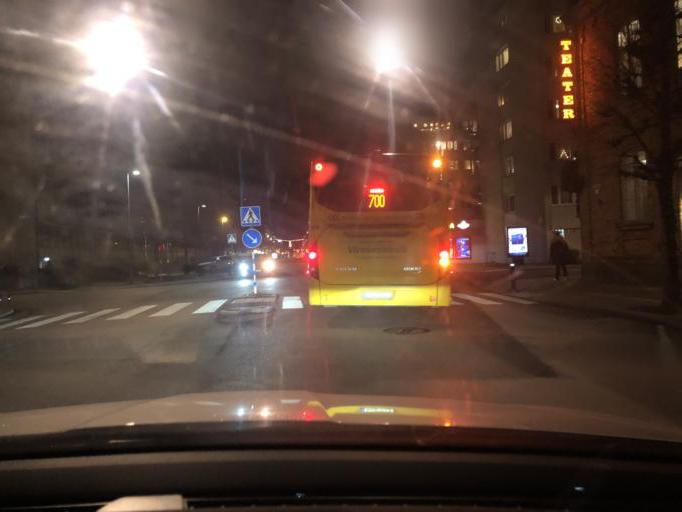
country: SE
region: Vaermland
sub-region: Karlstads Kommun
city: Karlstad
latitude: 59.3793
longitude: 13.4943
